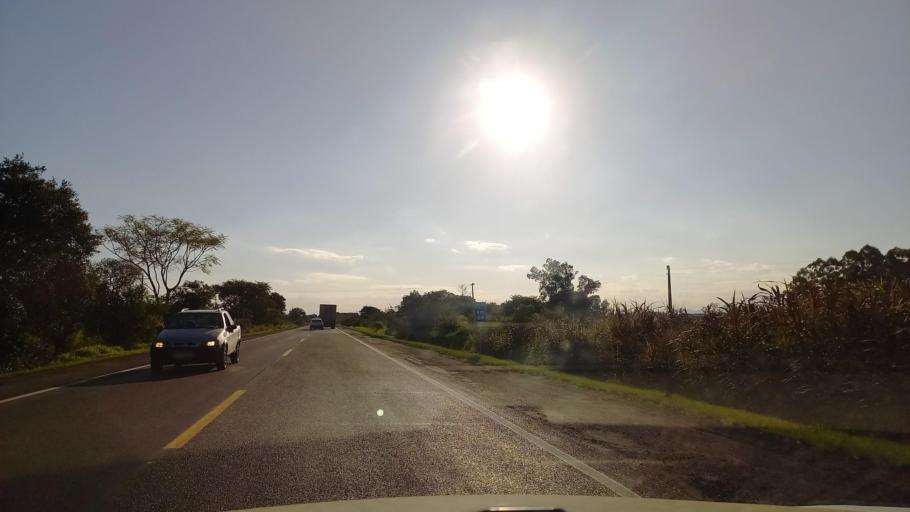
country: BR
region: Rio Grande do Sul
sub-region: Venancio Aires
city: Venancio Aires
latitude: -29.6649
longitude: -52.0546
